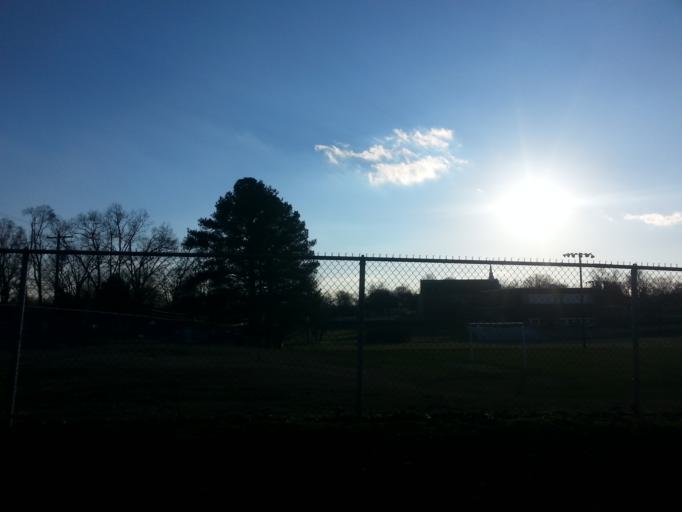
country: US
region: Tennessee
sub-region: Blount County
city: Maryville
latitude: 35.7675
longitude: -83.9526
